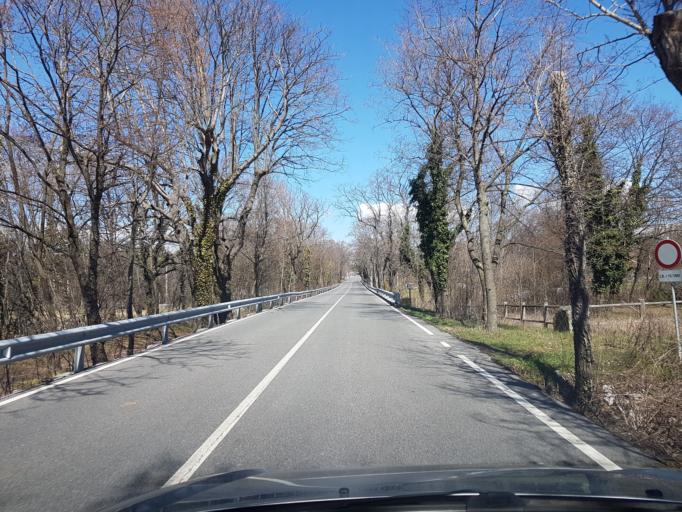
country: IT
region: Friuli Venezia Giulia
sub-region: Provincia di Trieste
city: Dolina
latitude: 45.6490
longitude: 13.8759
